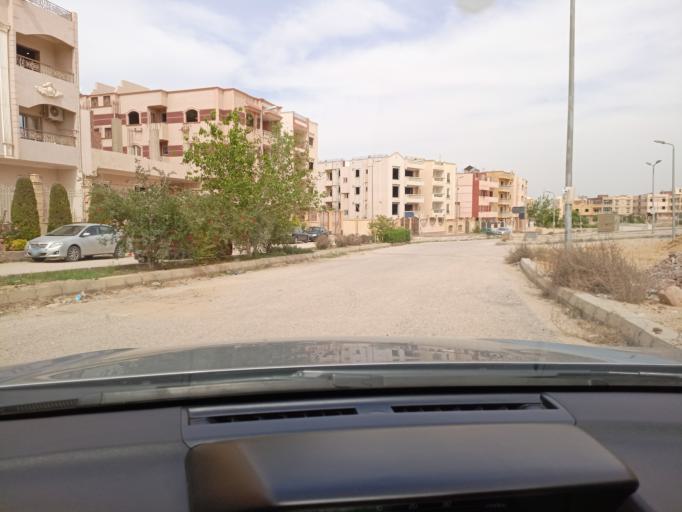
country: EG
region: Muhafazat al Qalyubiyah
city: Al Khankah
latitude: 30.2445
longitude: 31.4912
